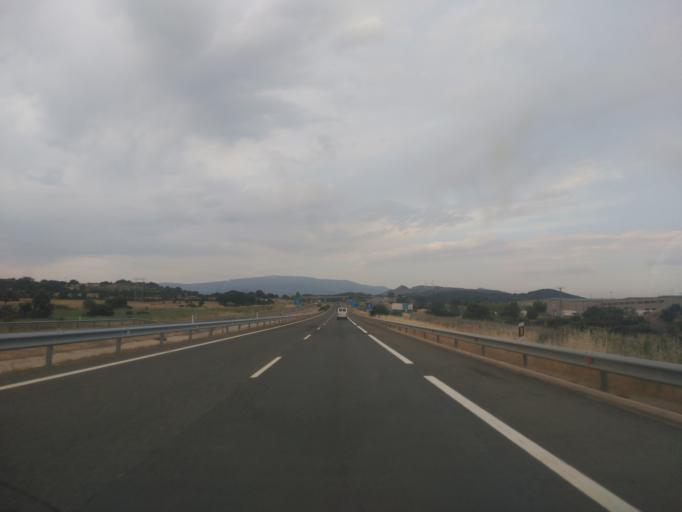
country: ES
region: Castille and Leon
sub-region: Provincia de Salamanca
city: Fuentes de Bejar
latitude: 40.5101
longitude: -5.6746
